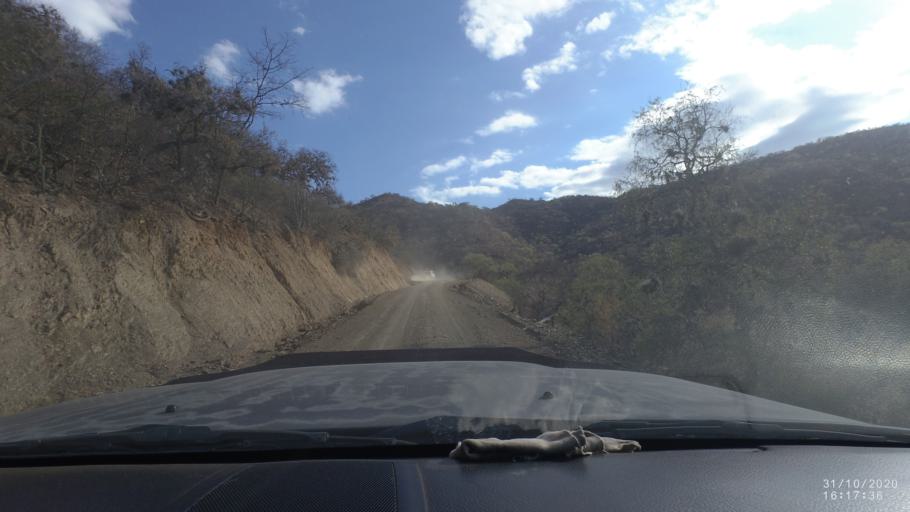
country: BO
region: Chuquisaca
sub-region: Provincia Zudanez
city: Mojocoya
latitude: -18.3912
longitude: -64.6044
